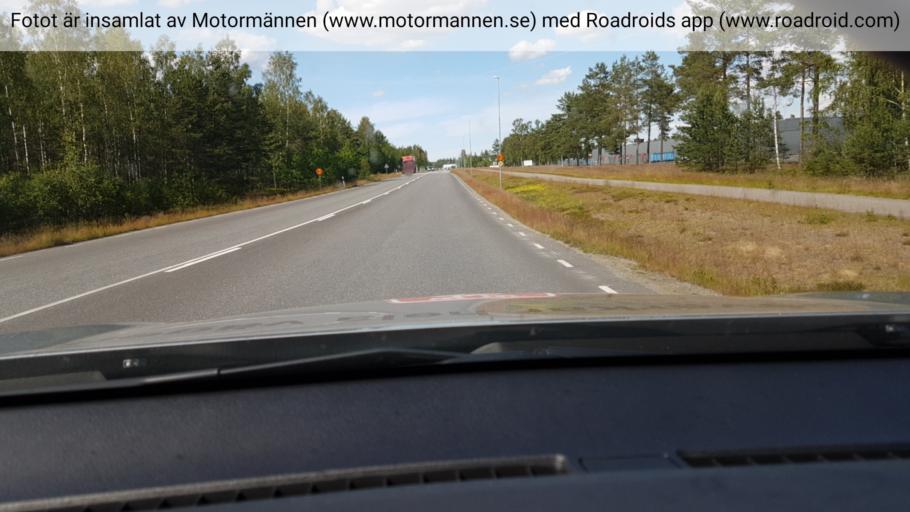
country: SE
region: Joenkoeping
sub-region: Vaggeryds Kommun
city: Skillingaryd
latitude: 57.4530
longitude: 14.0933
